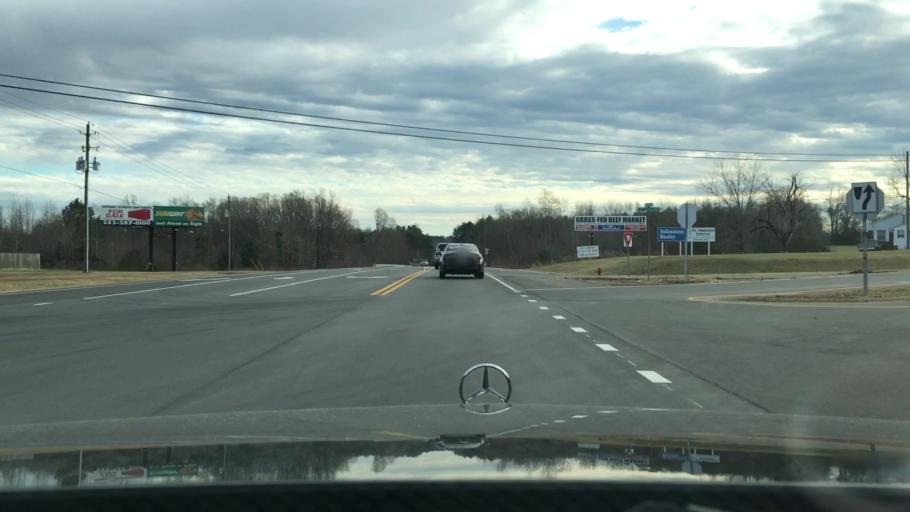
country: US
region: North Carolina
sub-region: Caswell County
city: Yanceyville
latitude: 36.4310
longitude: -79.3590
